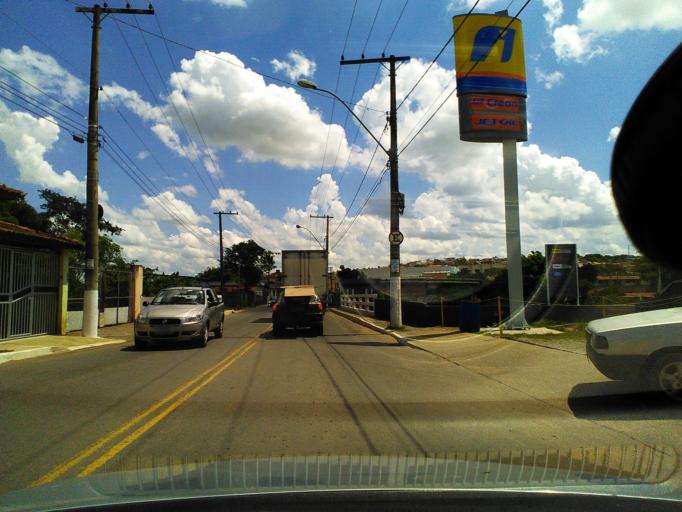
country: BR
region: Minas Gerais
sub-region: Tres Coracoes
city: Tres Coracoes
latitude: -21.7098
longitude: -45.2629
